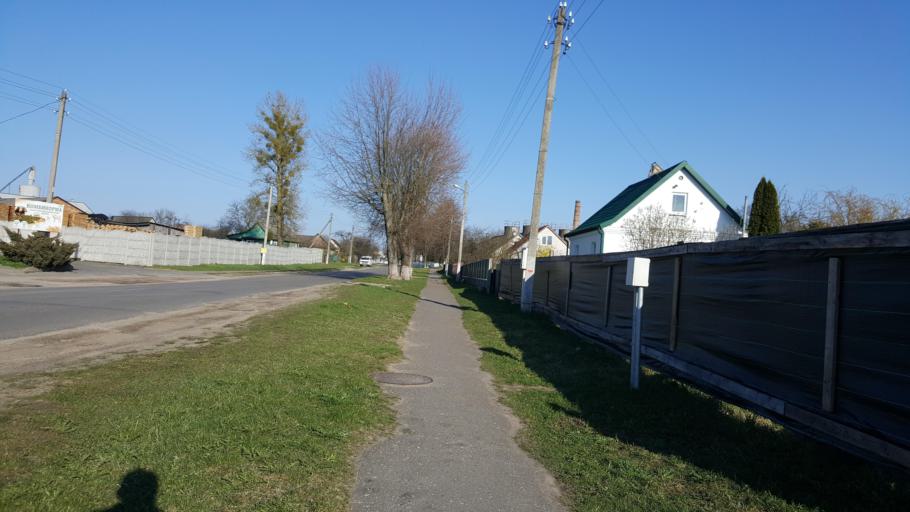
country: BY
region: Brest
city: Kamyanyets
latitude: 52.4027
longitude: 23.8311
